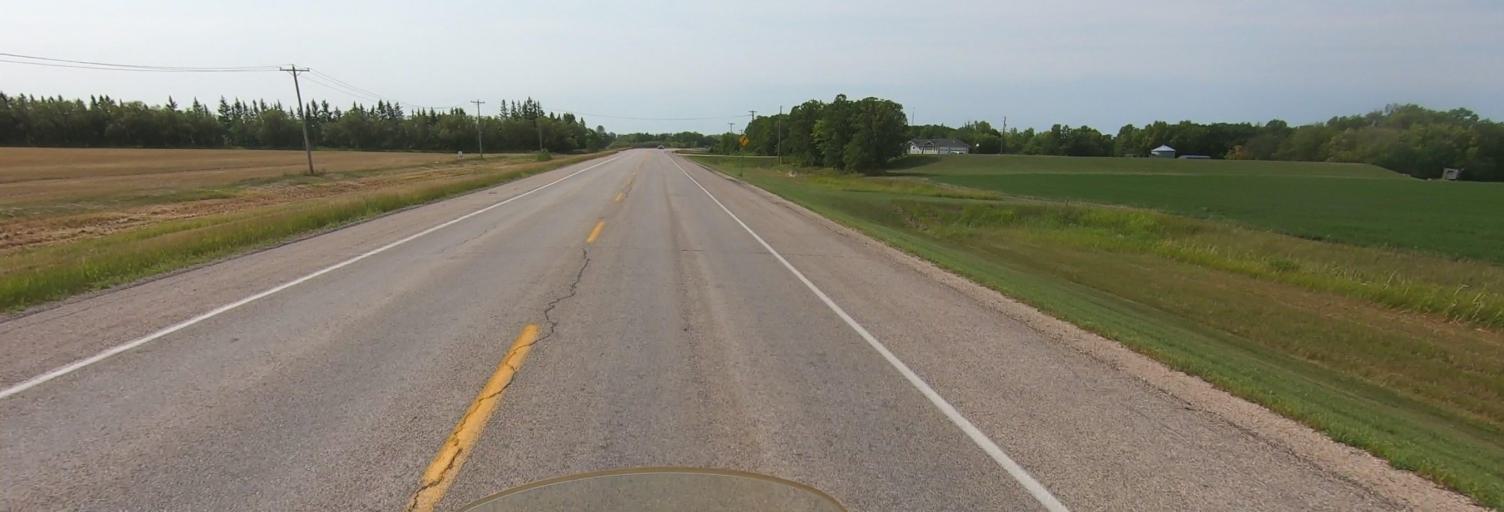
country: CA
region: Manitoba
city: Niverville
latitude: 49.6393
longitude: -97.1060
